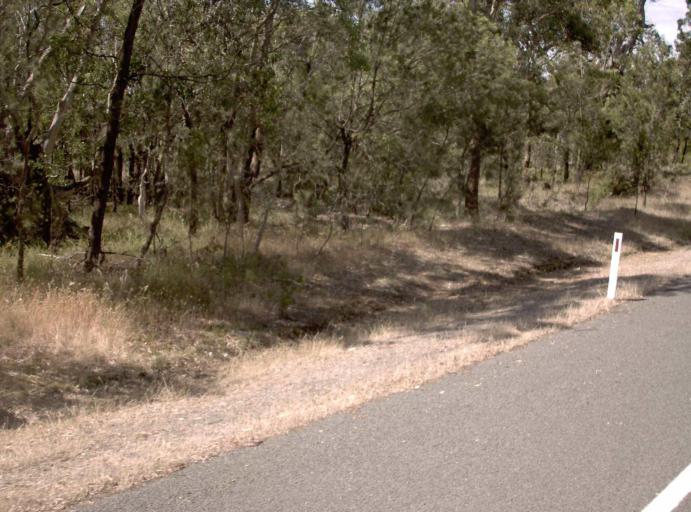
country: AU
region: Victoria
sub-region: Wellington
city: Sale
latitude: -37.9430
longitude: 147.1347
